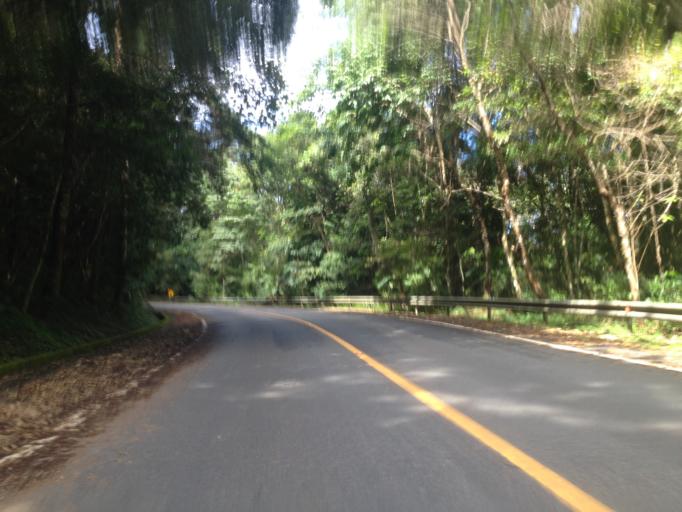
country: TH
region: Chiang Mai
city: Chiang Mai
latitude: 18.8009
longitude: 98.9059
